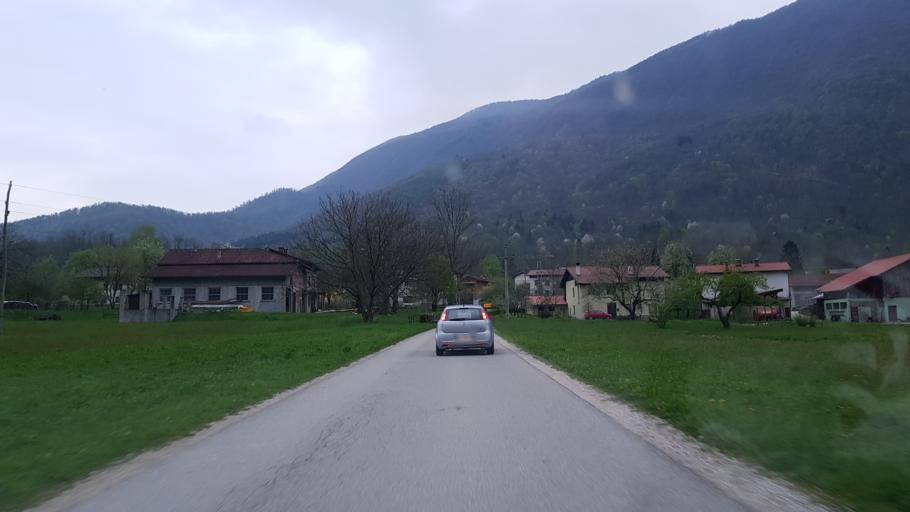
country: SI
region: Kobarid
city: Kobarid
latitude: 46.2443
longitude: 13.5526
